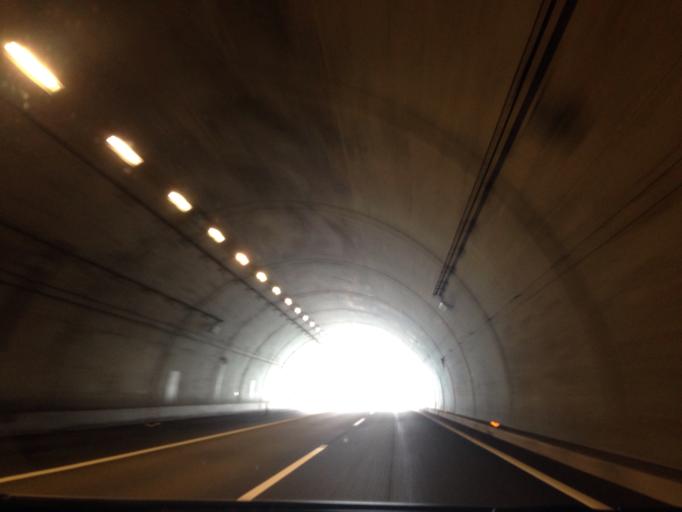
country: JP
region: Shizuoka
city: Fujinomiya
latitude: 35.1838
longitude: 138.6142
